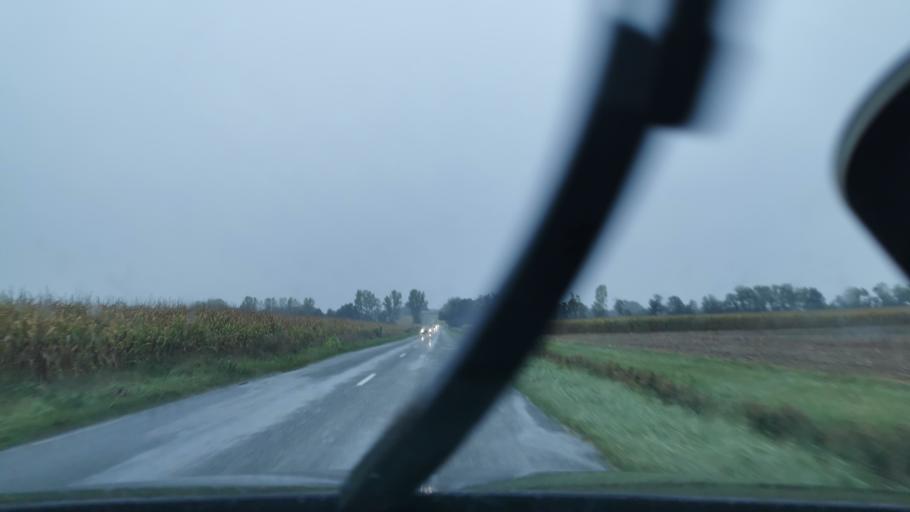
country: FR
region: Rhone-Alpes
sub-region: Departement de l'Ain
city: Civrieux
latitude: 45.9434
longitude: 4.8827
